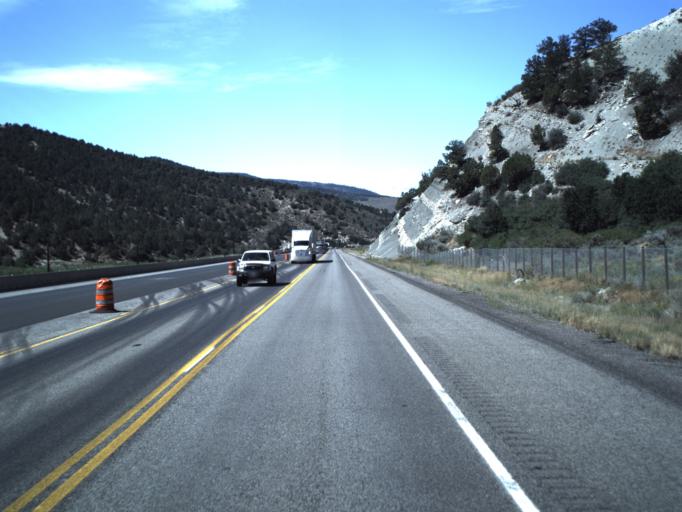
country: US
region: Utah
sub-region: Utah County
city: Mapleton
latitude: 39.9557
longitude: -111.2535
